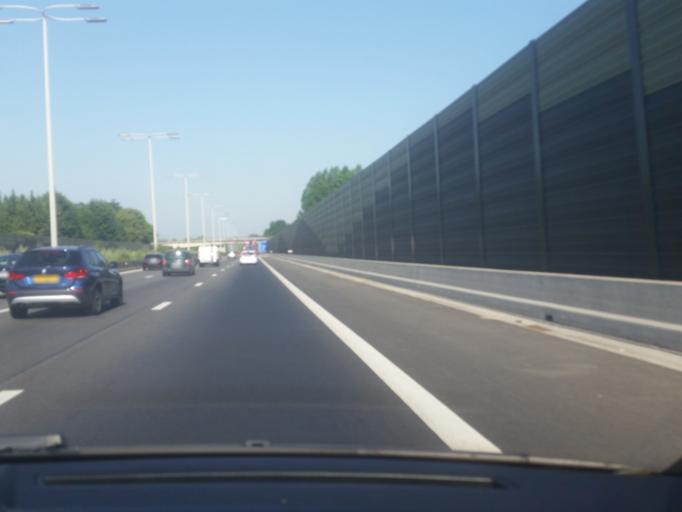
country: BE
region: Flanders
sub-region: Provincie Oost-Vlaanderen
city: Aalst
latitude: 50.9132
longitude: 4.0532
